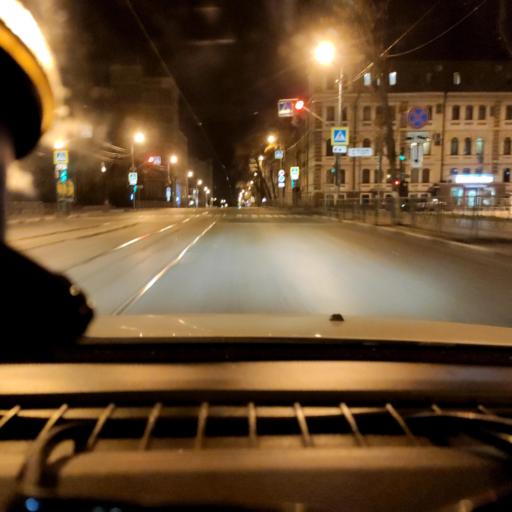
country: RU
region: Samara
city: Samara
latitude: 53.1938
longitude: 50.0994
